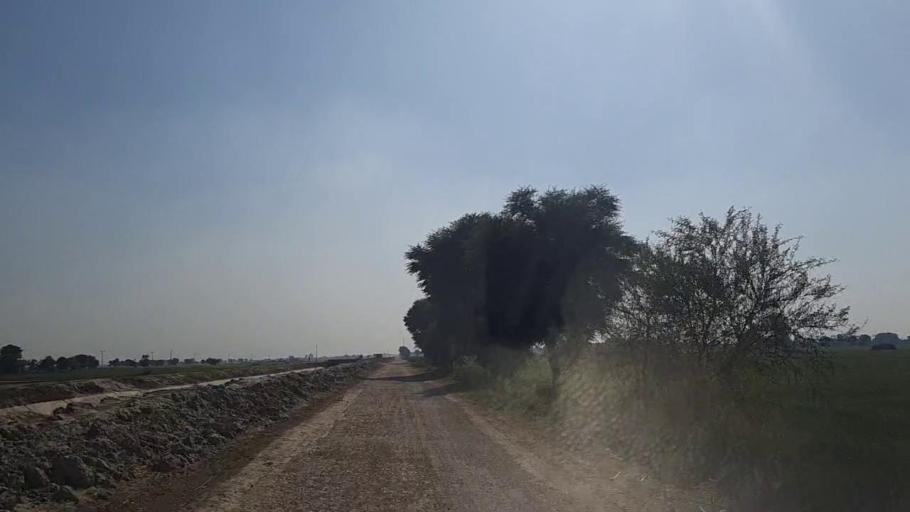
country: PK
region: Sindh
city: Shahpur Chakar
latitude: 26.2111
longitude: 68.5839
